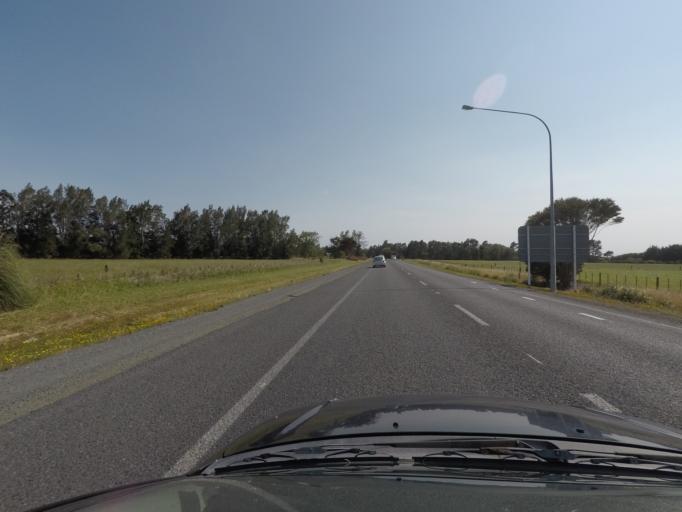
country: NZ
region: Northland
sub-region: Whangarei
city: Ruakaka
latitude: -35.9626
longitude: 174.4471
